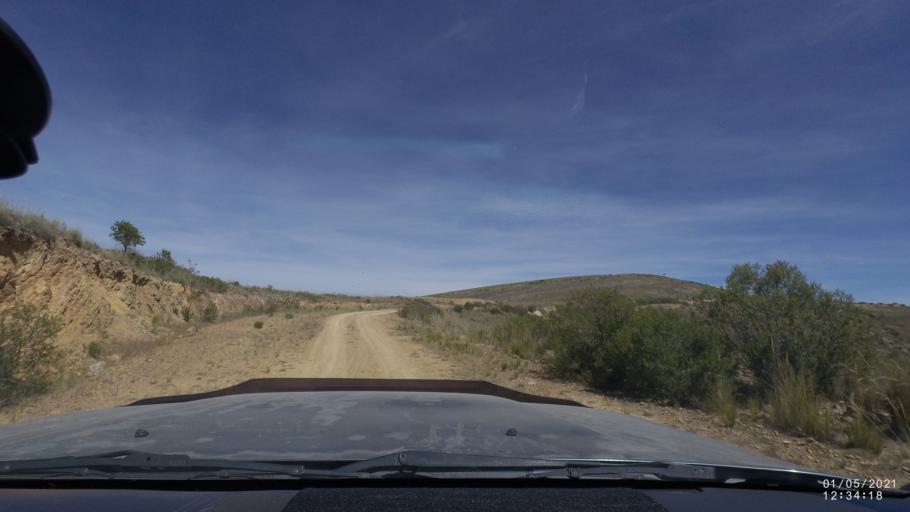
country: BO
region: Cochabamba
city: Capinota
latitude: -17.6762
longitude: -66.1503
